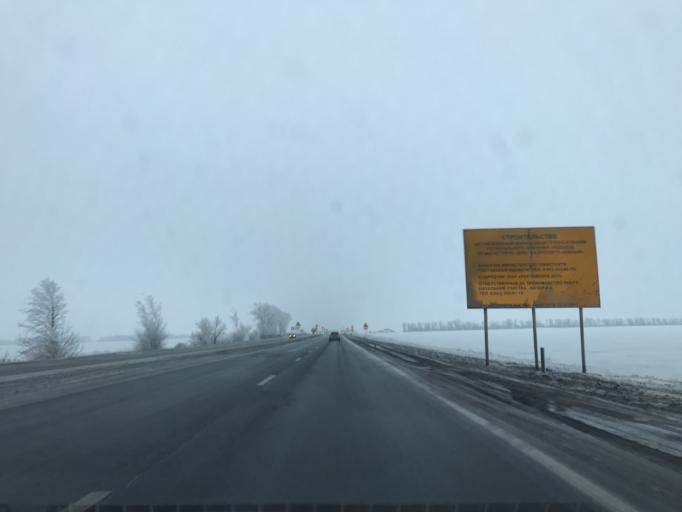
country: RU
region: Rostov
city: Grushevskaya
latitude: 47.4948
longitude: 39.9707
